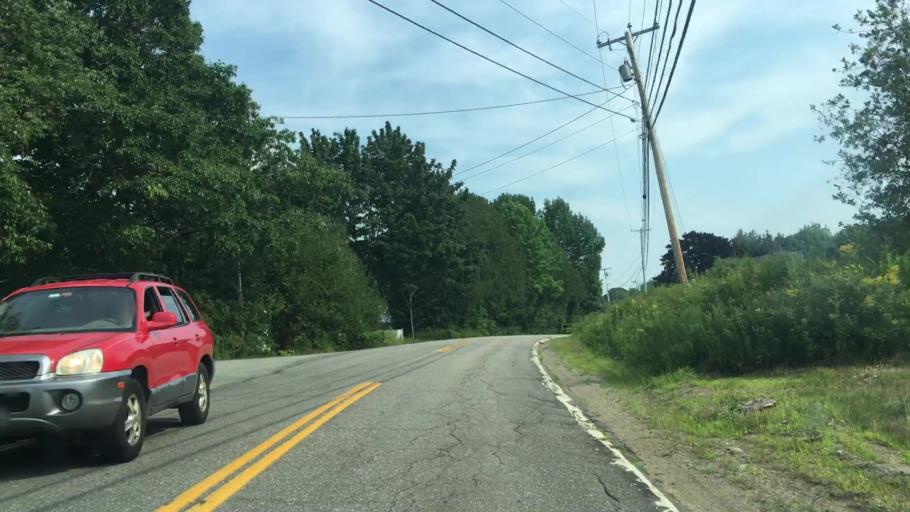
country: US
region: Maine
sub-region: Lincoln County
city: Waldoboro
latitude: 44.0646
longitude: -69.3469
